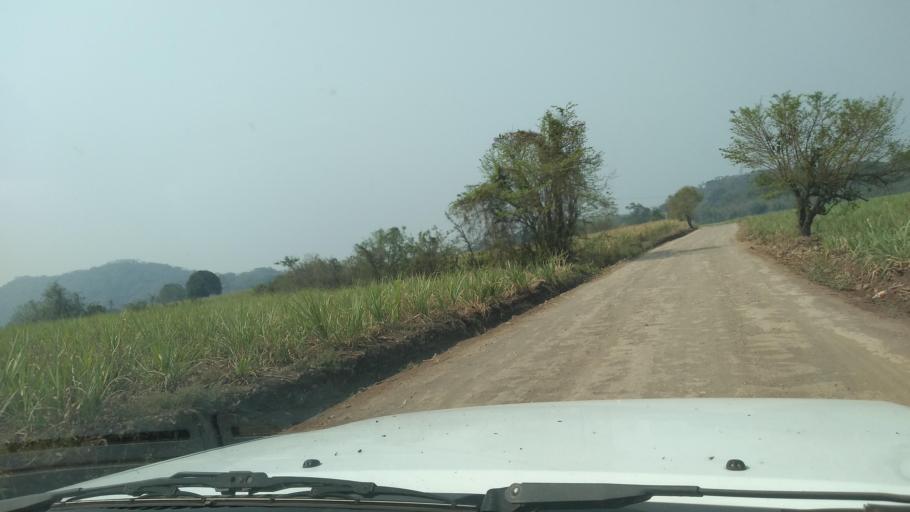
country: MX
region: Oaxaca
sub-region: Cosolapa
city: Cosolapa
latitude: 18.6174
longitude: -96.6312
